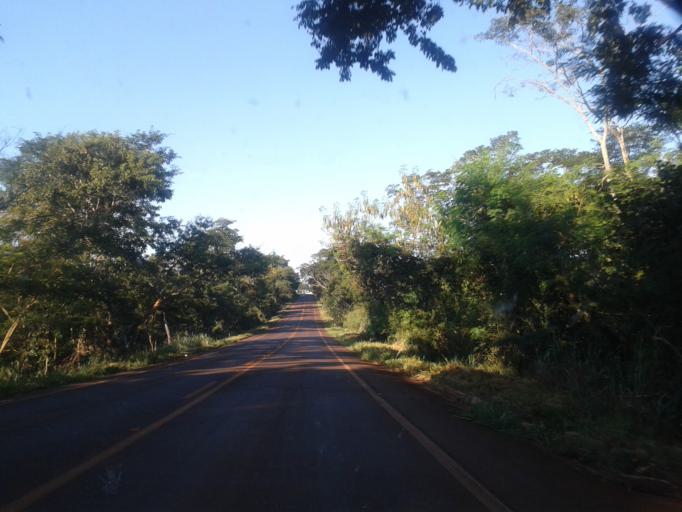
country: BR
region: Minas Gerais
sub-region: Capinopolis
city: Capinopolis
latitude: -18.6890
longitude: -49.6109
